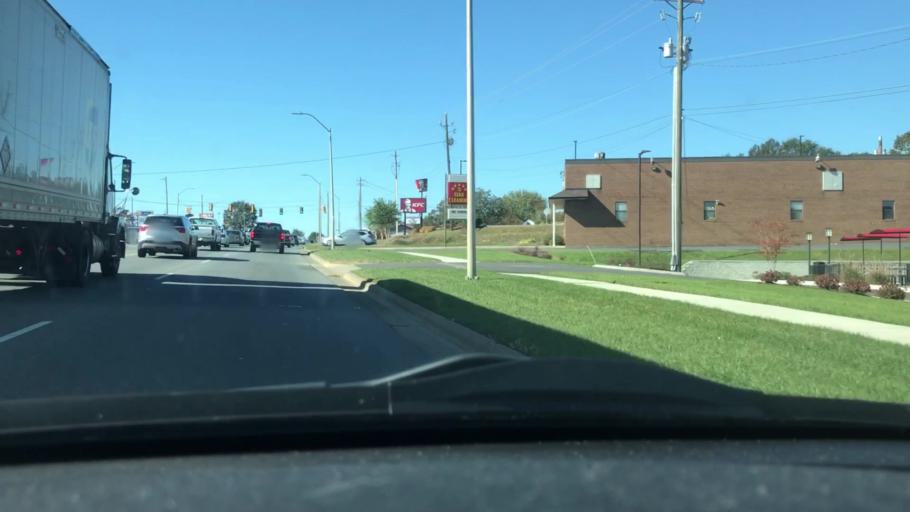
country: US
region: North Carolina
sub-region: Randolph County
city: Asheboro
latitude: 35.6903
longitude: -79.8045
